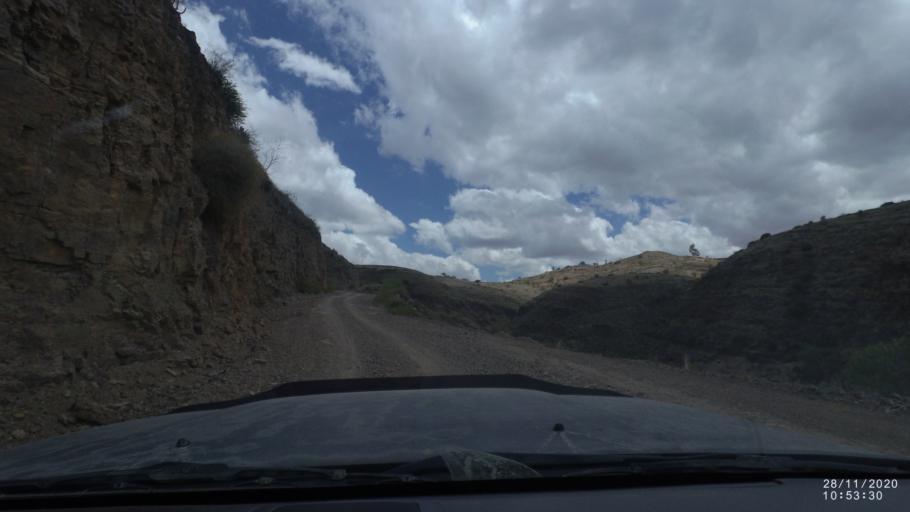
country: BO
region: Cochabamba
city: Capinota
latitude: -17.7808
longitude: -66.1189
